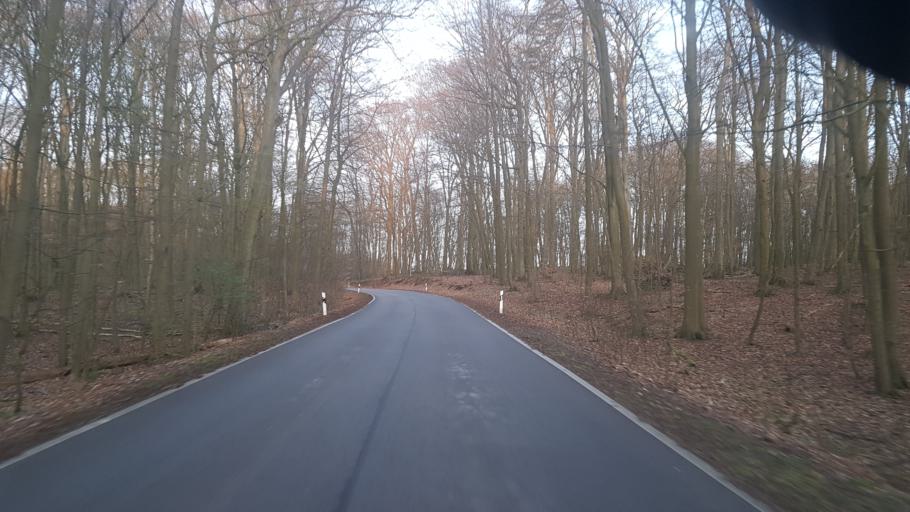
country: DE
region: Brandenburg
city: Gramzow
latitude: 53.1873
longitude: 13.9222
